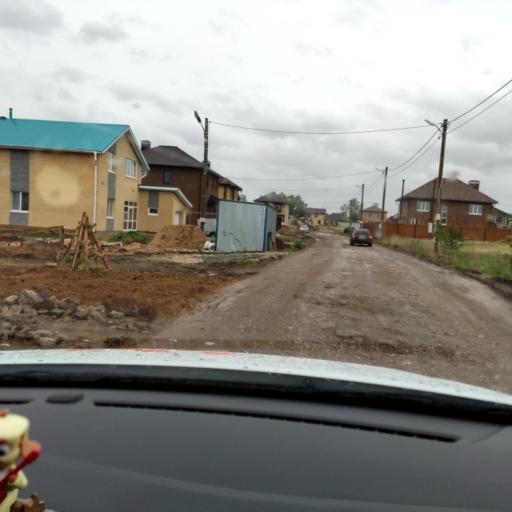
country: RU
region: Tatarstan
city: Vysokaya Gora
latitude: 55.7901
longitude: 49.2592
